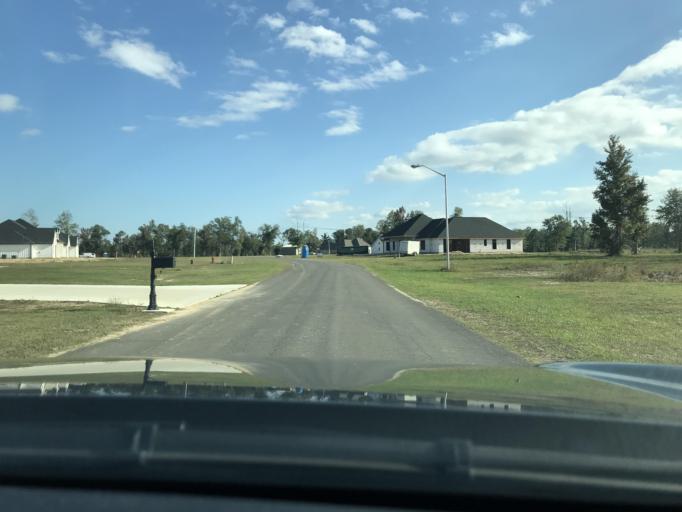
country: US
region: Louisiana
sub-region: Calcasieu Parish
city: Moss Bluff
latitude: 30.3346
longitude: -93.2497
